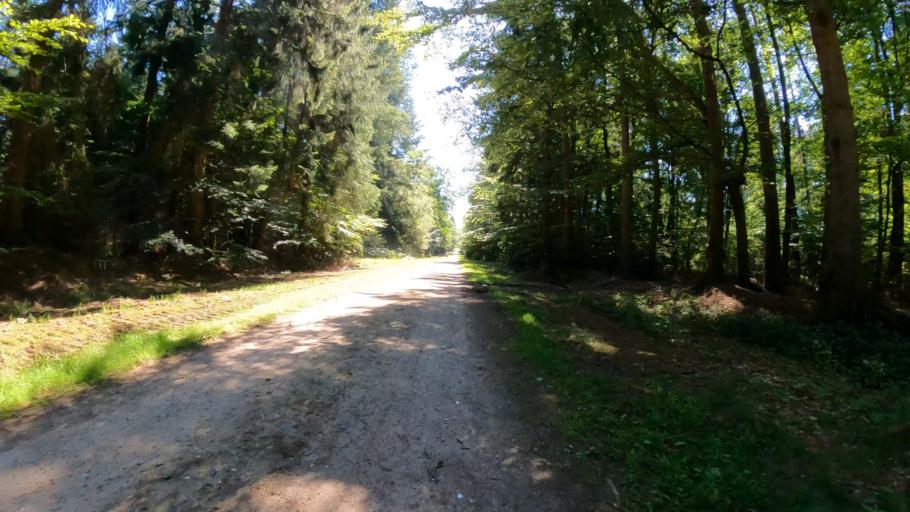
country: DE
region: Schleswig-Holstein
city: Aumuhle
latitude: 53.5160
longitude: 10.3363
